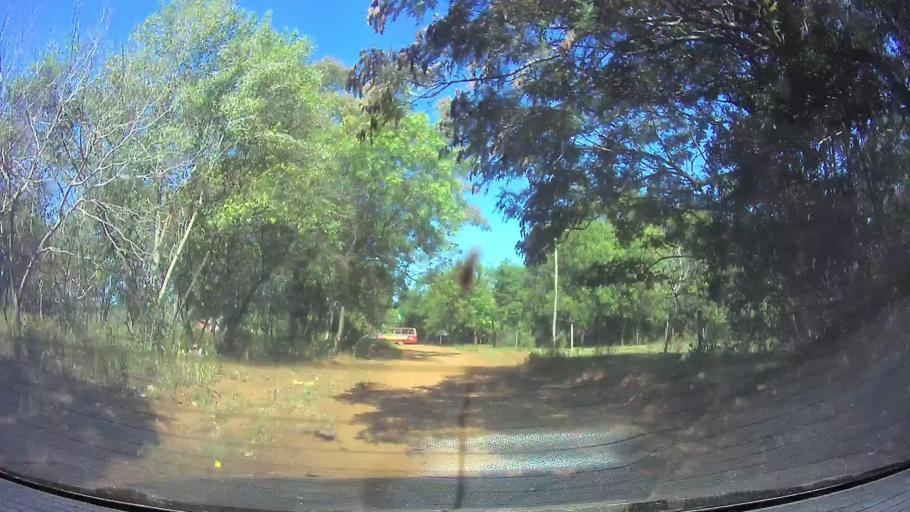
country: PY
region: Central
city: Limpio
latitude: -25.2415
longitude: -57.4541
